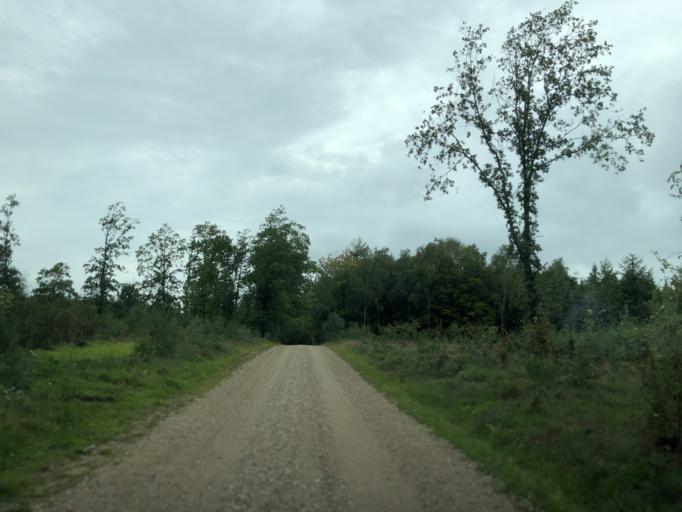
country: DK
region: Central Jutland
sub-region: Holstebro Kommune
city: Holstebro
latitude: 56.2396
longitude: 8.5128
